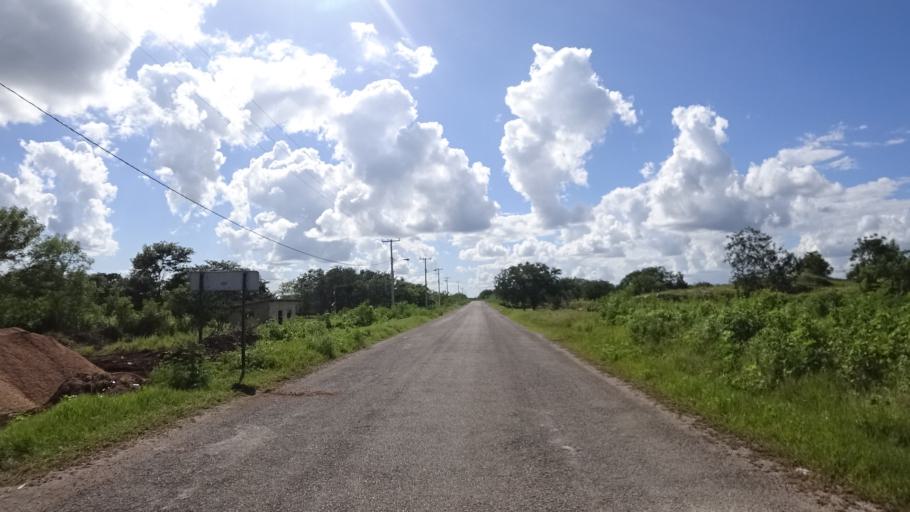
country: MX
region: Yucatan
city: Muna
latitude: 20.6472
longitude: -89.6916
